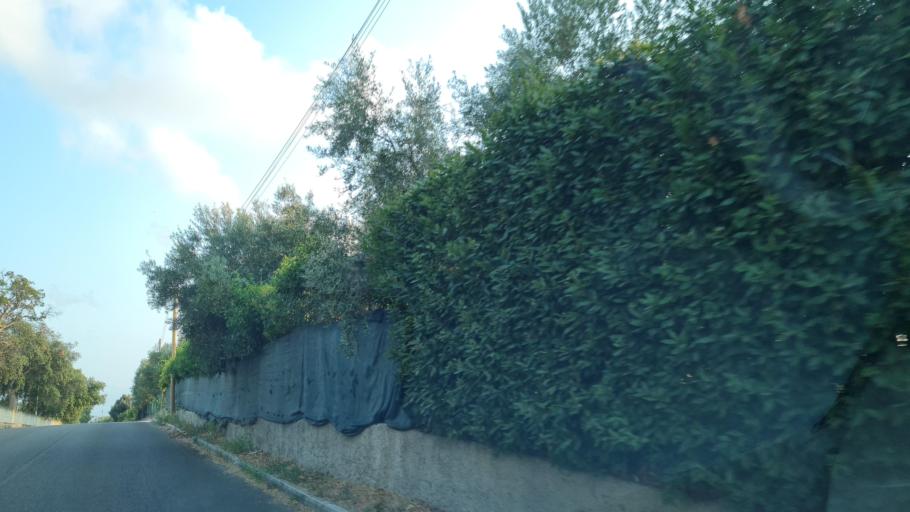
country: IT
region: Latium
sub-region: Provincia di Viterbo
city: Montalto di Castro
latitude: 42.3396
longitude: 11.6120
